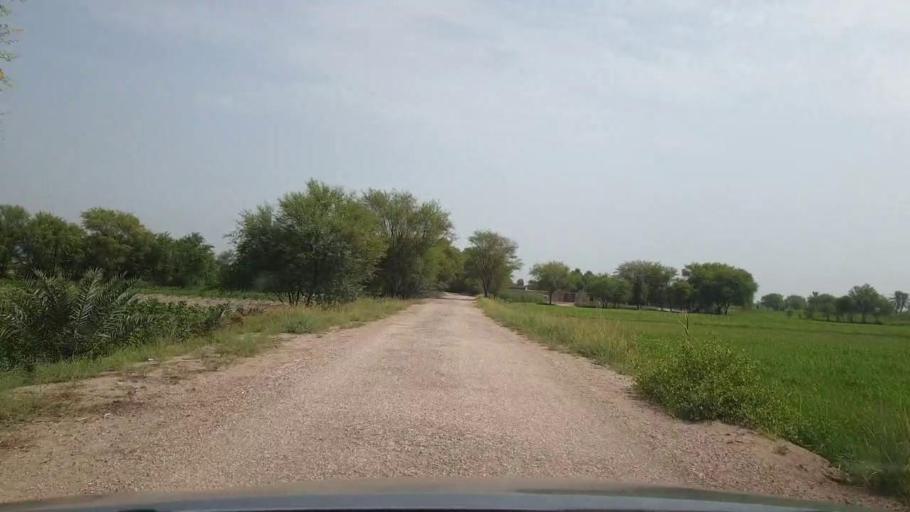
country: PK
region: Sindh
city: Rohri
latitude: 27.6521
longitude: 69.0236
